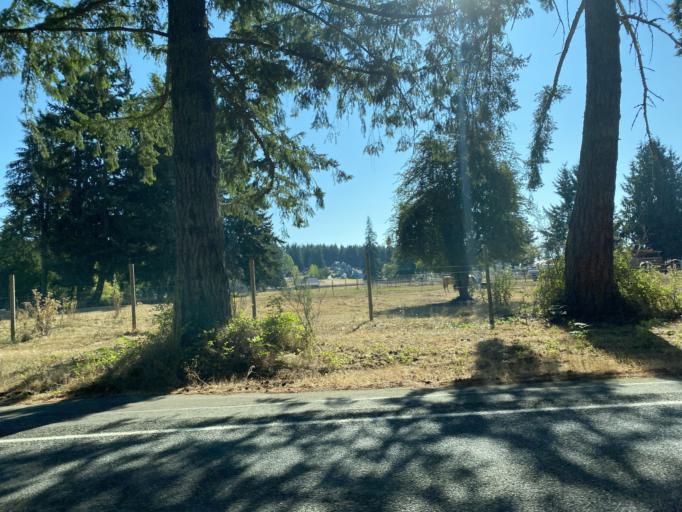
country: US
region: Washington
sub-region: Thurston County
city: Tanglewilde-Thompson Place
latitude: 46.9704
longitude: -122.7640
